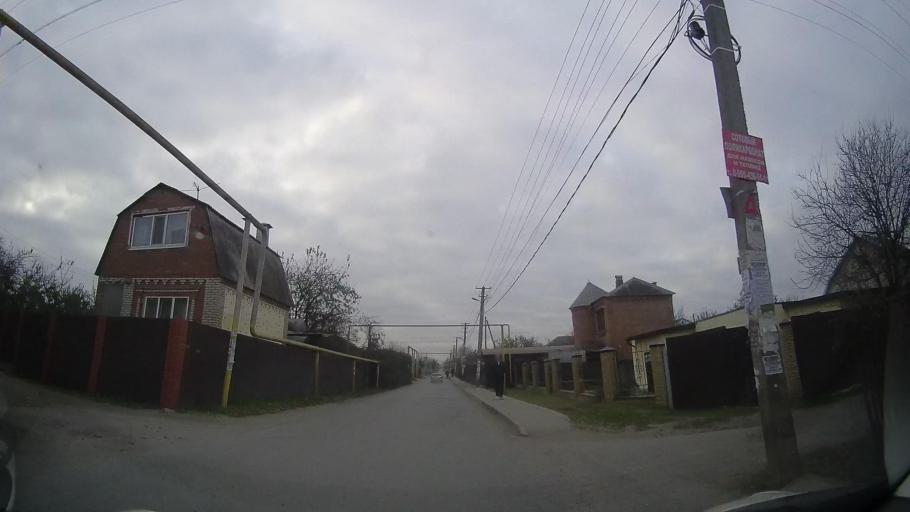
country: RU
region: Rostov
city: Bataysk
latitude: 47.0845
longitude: 39.7612
